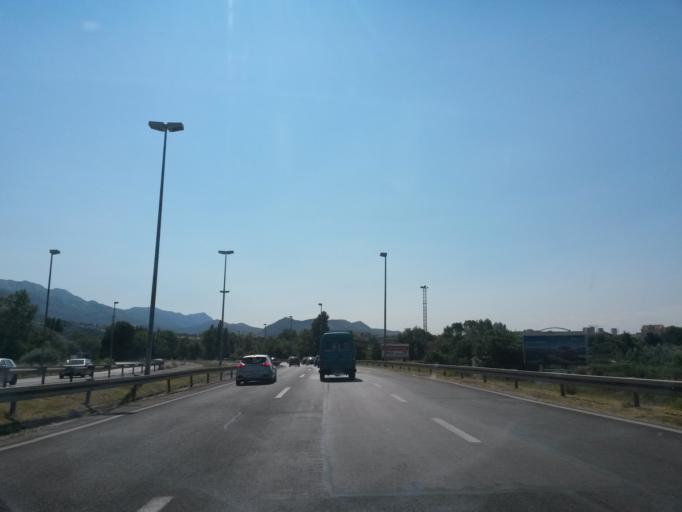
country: HR
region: Splitsko-Dalmatinska
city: Vranjic
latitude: 43.5354
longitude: 16.4807
